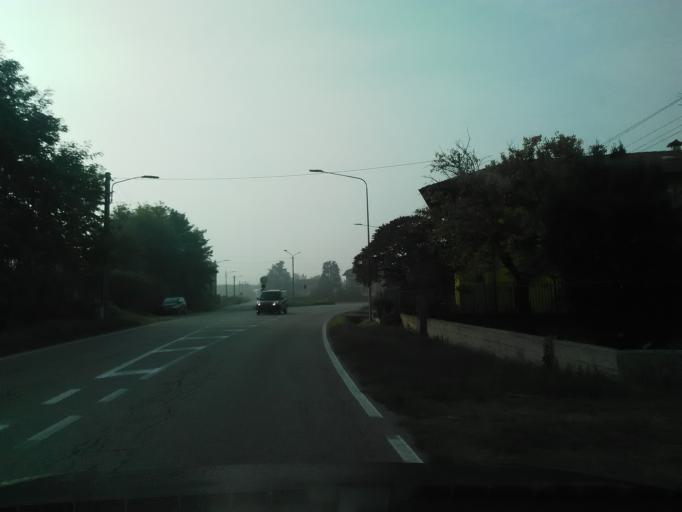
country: IT
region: Piedmont
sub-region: Provincia di Vercelli
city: Santhia
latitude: 45.3578
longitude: 8.1723
